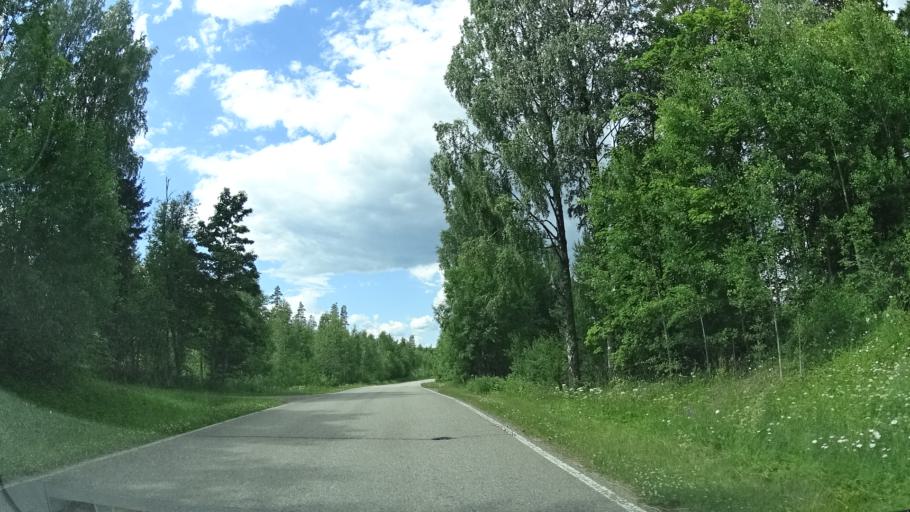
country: FI
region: Uusimaa
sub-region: Helsinki
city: Espoo
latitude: 60.4119
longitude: 24.5676
